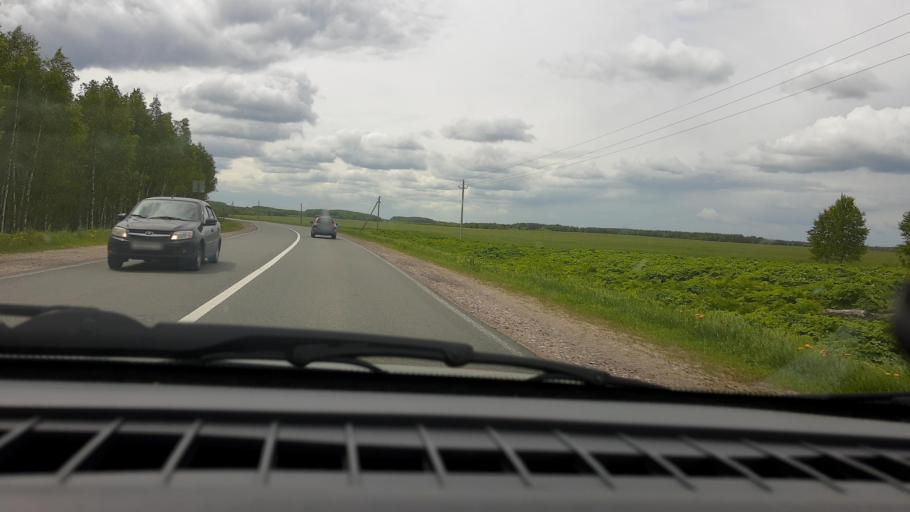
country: RU
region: Nizjnij Novgorod
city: Sukhobezvodnoye
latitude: 56.8536
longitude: 44.7640
